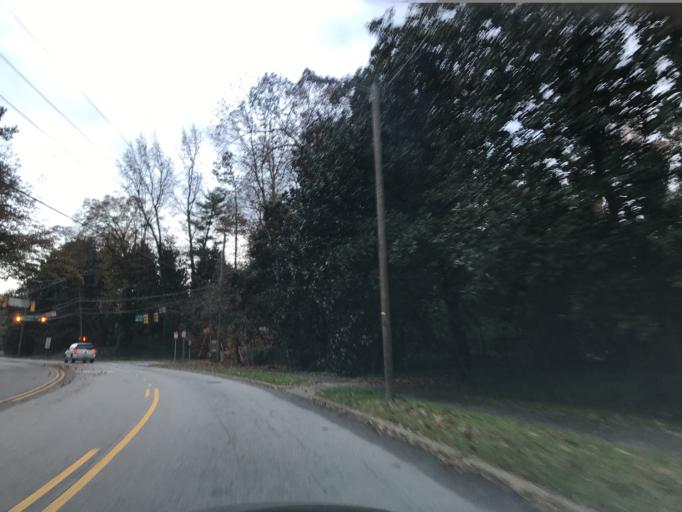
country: US
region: North Carolina
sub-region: Wake County
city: West Raleigh
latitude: 35.8232
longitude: -78.6511
